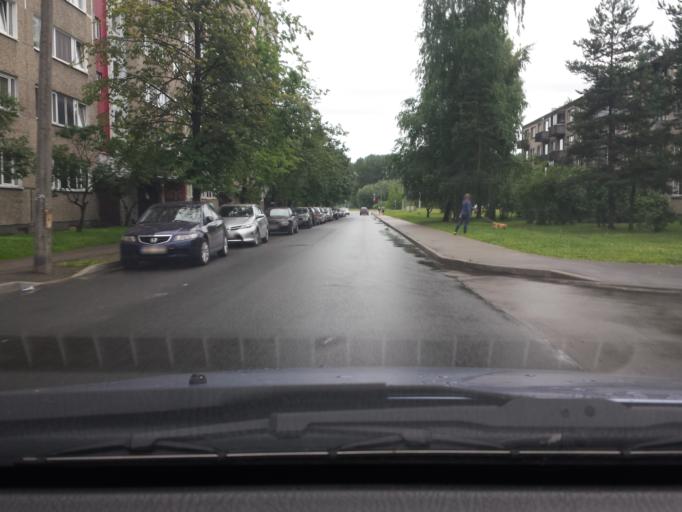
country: LV
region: Kekava
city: Kekava
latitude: 56.9013
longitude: 24.2056
